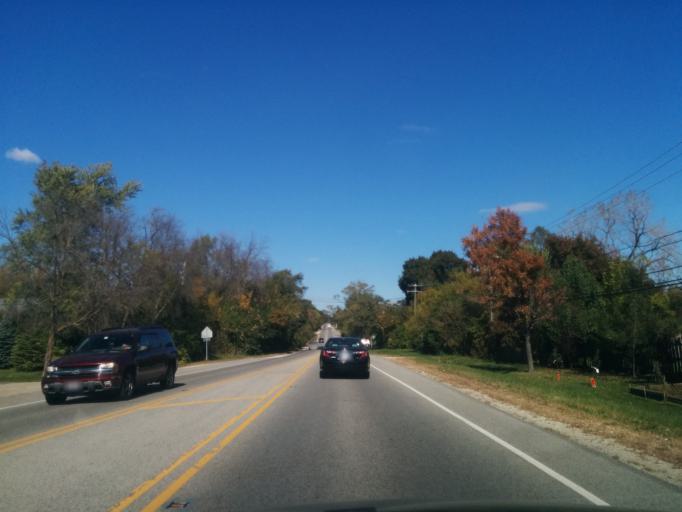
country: US
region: Illinois
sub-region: DuPage County
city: Glen Ellyn
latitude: 41.8452
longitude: -88.0531
